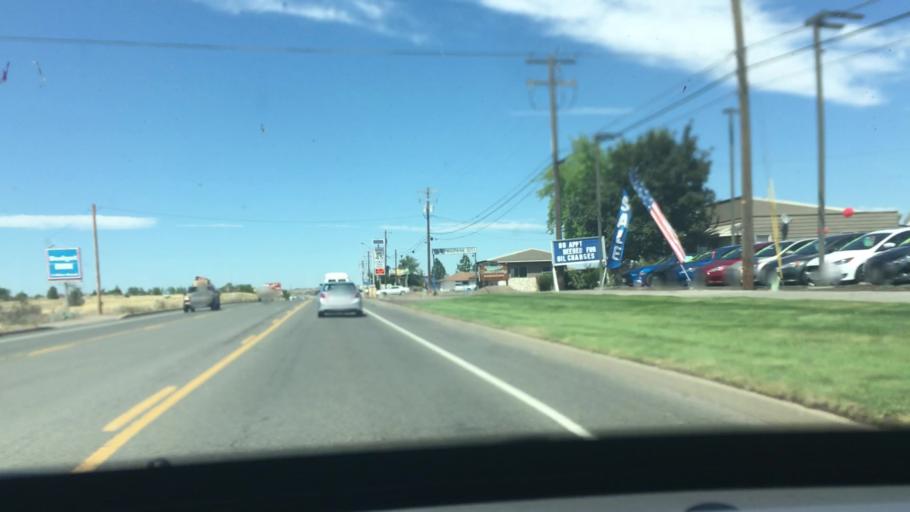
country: US
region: Oregon
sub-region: Jefferson County
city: Madras
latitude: 44.6111
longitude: -121.1370
